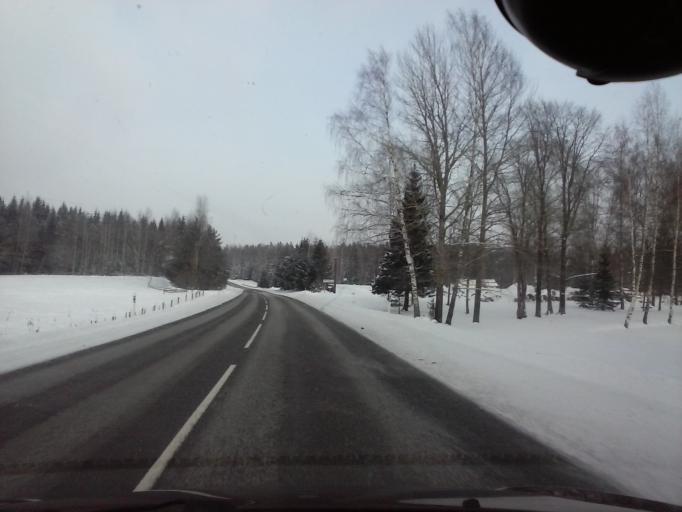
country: EE
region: Paernumaa
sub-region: Saarde vald
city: Kilingi-Nomme
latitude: 58.1799
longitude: 25.0478
